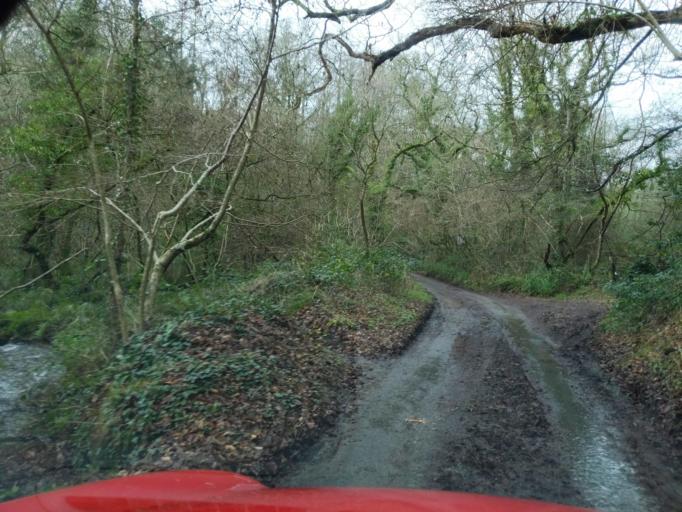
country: GB
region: England
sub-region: Cornwall
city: Duloe
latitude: 50.3461
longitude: -4.5222
